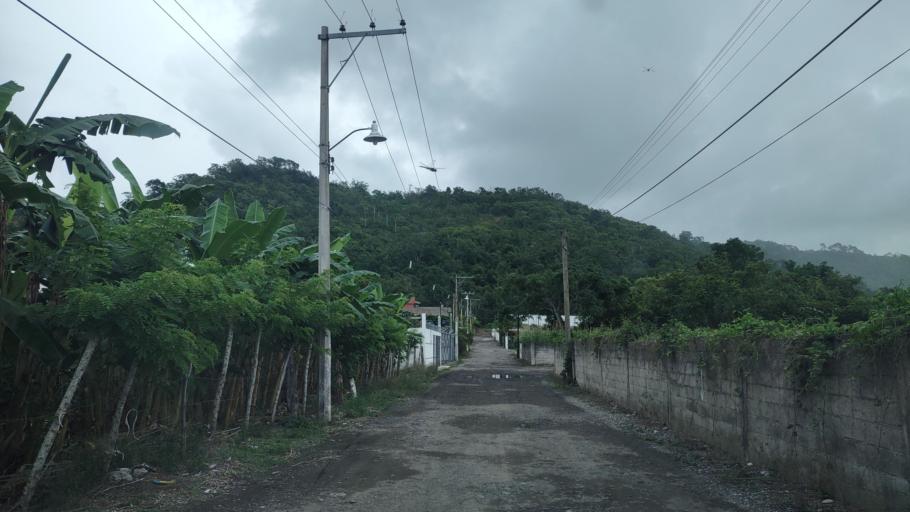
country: MX
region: Veracruz
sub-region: Papantla
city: Fraccionamiento la Florida
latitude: 20.5862
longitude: -97.4246
